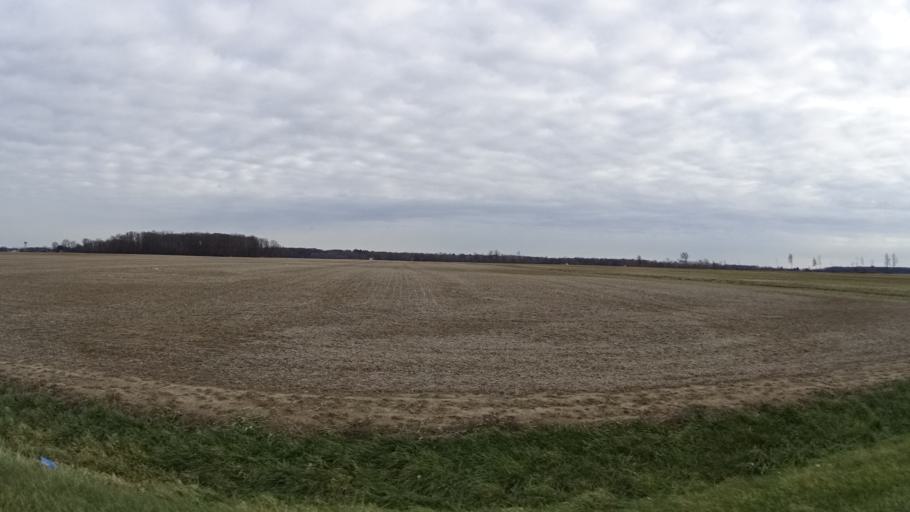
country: US
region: Ohio
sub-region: Lorain County
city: Camden
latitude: 41.2476
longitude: -82.3317
